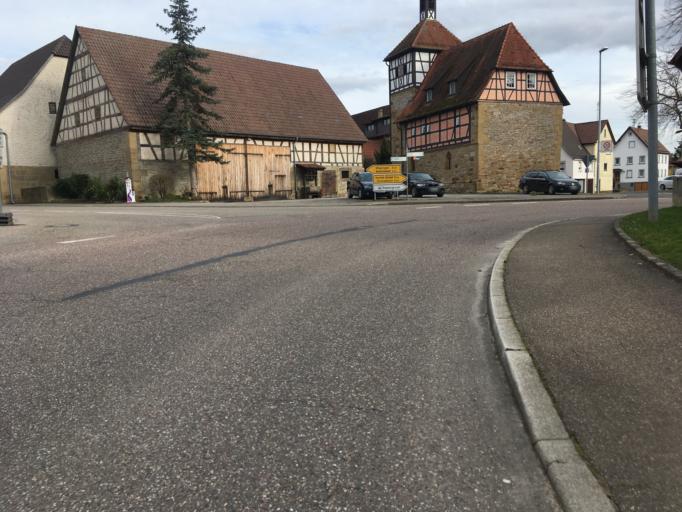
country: DE
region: Baden-Wuerttemberg
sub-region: Regierungsbezirk Stuttgart
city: Bretzfeld
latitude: 49.2160
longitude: 9.4063
